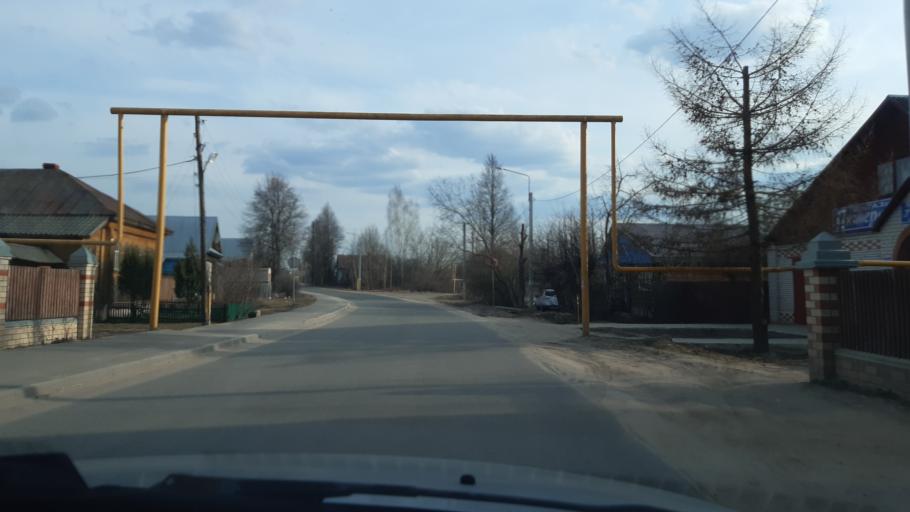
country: RU
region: Vladimir
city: Nikologory
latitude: 56.1381
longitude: 41.9908
